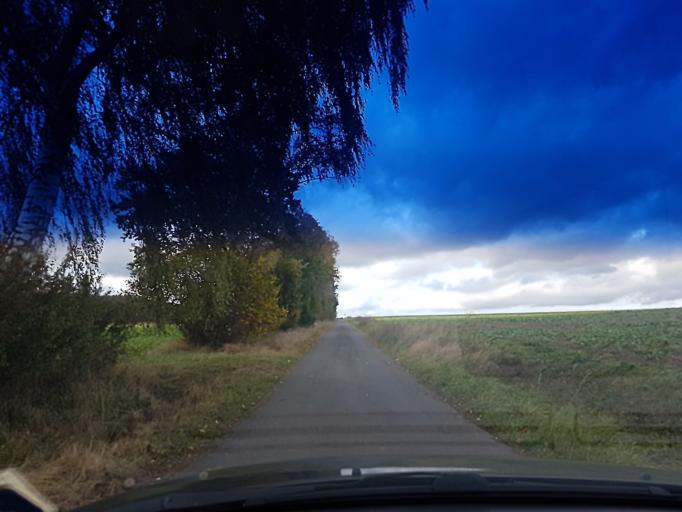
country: DE
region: Bavaria
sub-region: Regierungsbezirk Mittelfranken
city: Wachenroth
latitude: 49.7520
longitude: 10.6805
